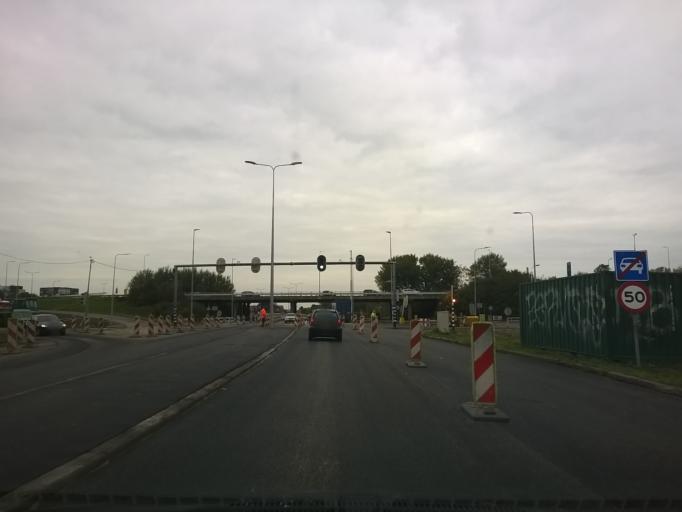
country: NL
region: Groningen
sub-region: Gemeente Groningen
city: Korrewegwijk
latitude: 53.2332
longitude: 6.5290
